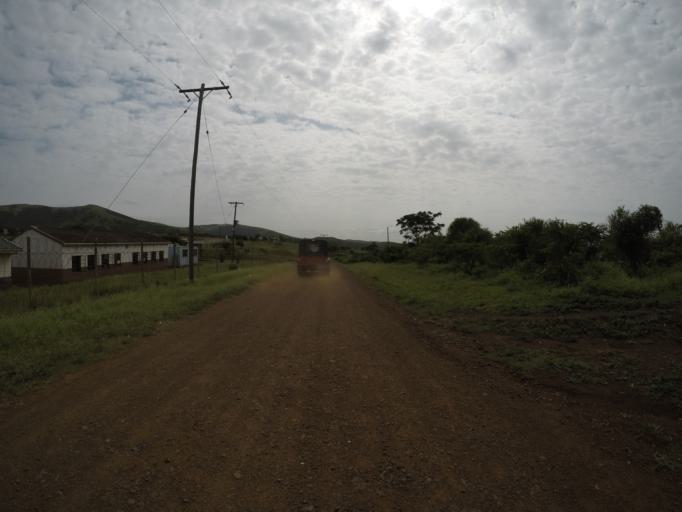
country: ZA
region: KwaZulu-Natal
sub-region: uThungulu District Municipality
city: Empangeni
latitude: -28.6213
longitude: 31.9043
